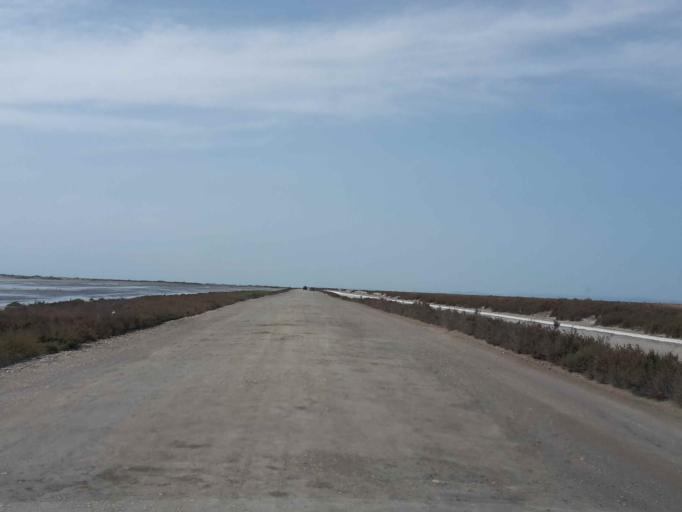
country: FR
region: Provence-Alpes-Cote d'Azur
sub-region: Departement des Bouches-du-Rhone
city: Port-Saint-Louis-du-Rhone
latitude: 43.4087
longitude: 4.6574
